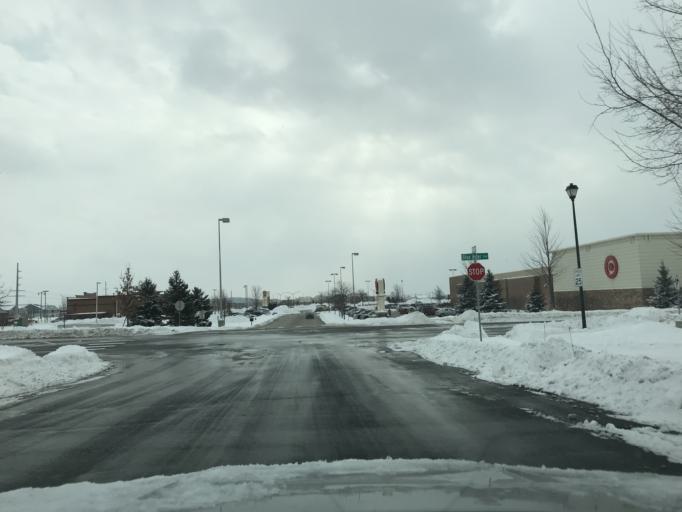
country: US
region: Wisconsin
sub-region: Dane County
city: Sun Prairie
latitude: 43.1720
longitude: -89.2667
